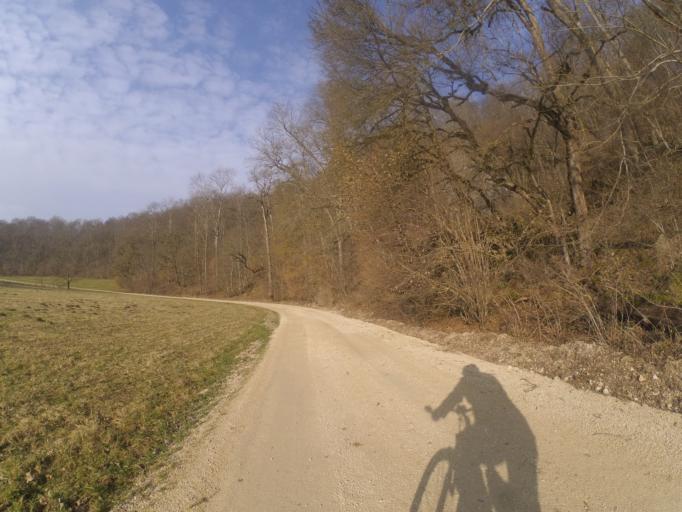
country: DE
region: Baden-Wuerttemberg
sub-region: Tuebingen Region
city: Rechtenstein
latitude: 48.2709
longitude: 9.5313
